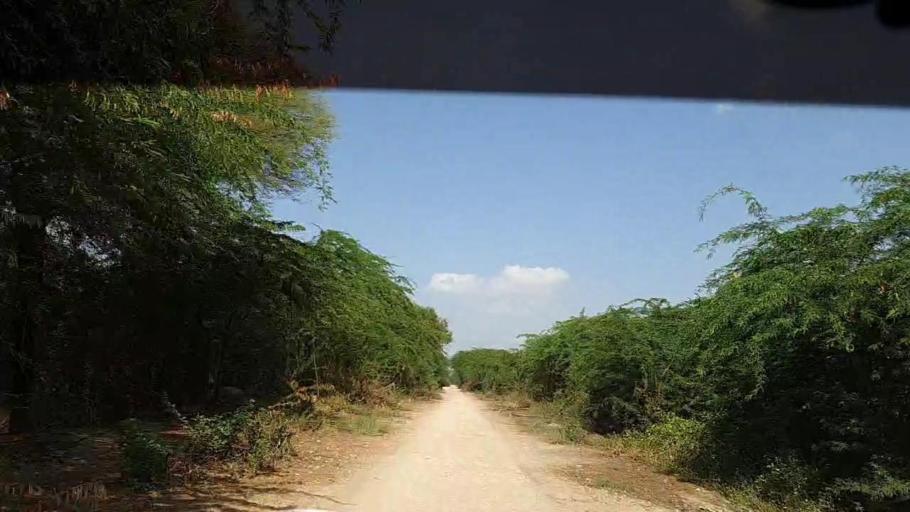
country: PK
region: Sindh
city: Badin
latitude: 24.5883
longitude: 68.7942
